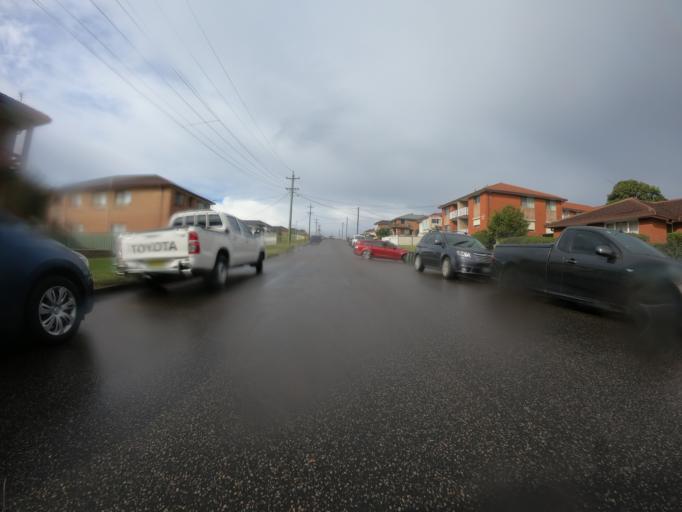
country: AU
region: New South Wales
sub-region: Wollongong
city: Port Kembla
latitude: -34.4901
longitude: 150.8899
